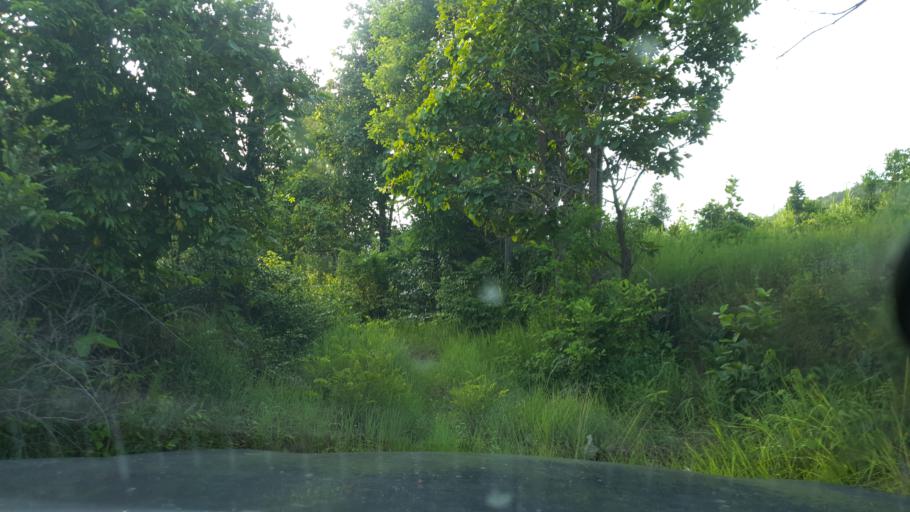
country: TH
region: Lamphun
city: Ban Thi
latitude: 18.6710
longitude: 99.1683
